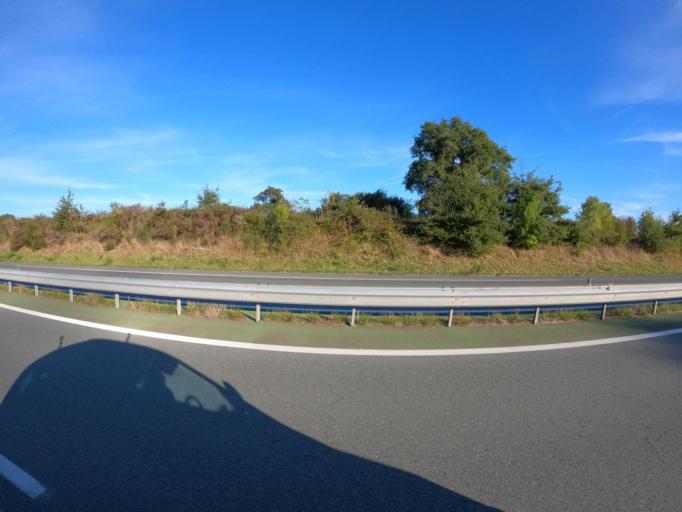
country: FR
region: Pays de la Loire
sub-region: Departement de Maine-et-Loire
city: Chemille-Melay
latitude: 47.1897
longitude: -0.7763
